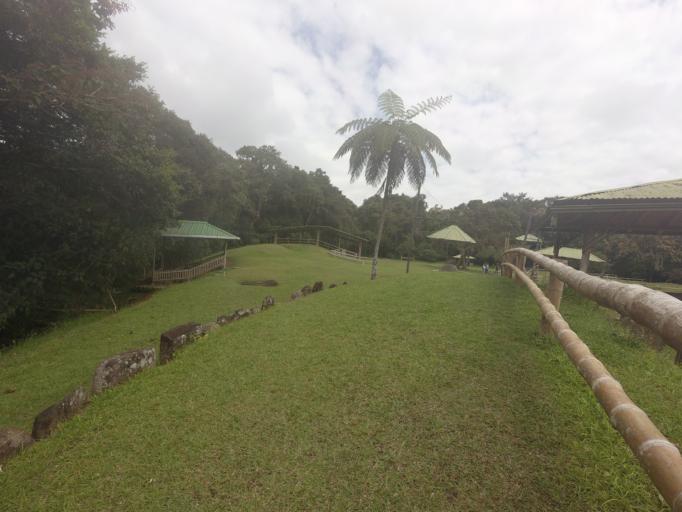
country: CO
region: Huila
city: San Agustin
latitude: 1.8842
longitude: -76.2964
